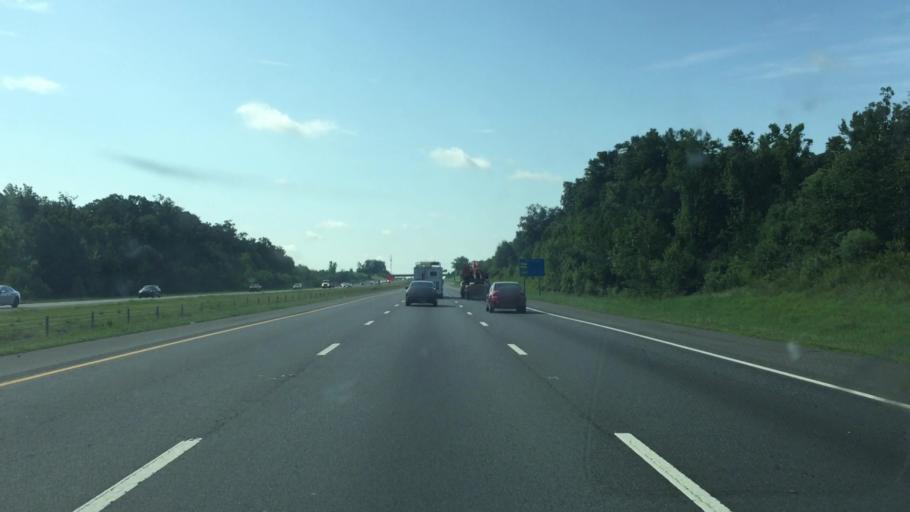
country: US
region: North Carolina
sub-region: Cabarrus County
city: Harrisburg
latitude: 35.2938
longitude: -80.6814
